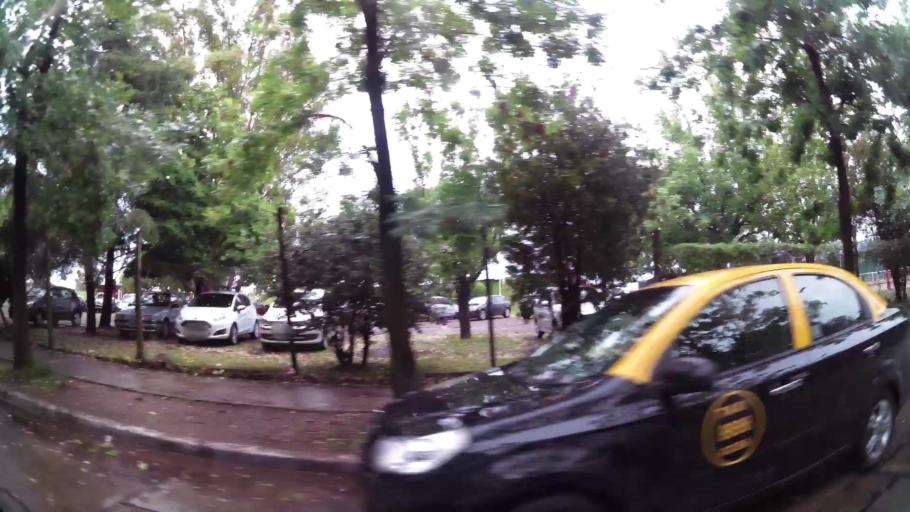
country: AR
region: Buenos Aires F.D.
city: Villa Lugano
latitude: -34.6532
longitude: -58.4473
